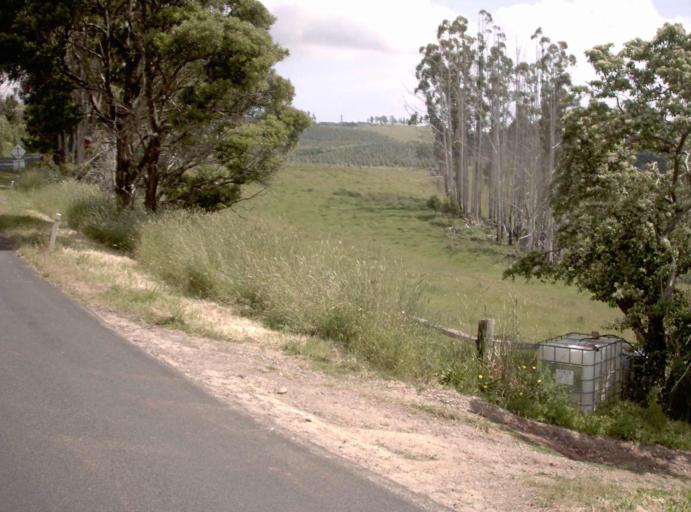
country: AU
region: Victoria
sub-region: Latrobe
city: Traralgon
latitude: -38.3492
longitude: 146.5688
